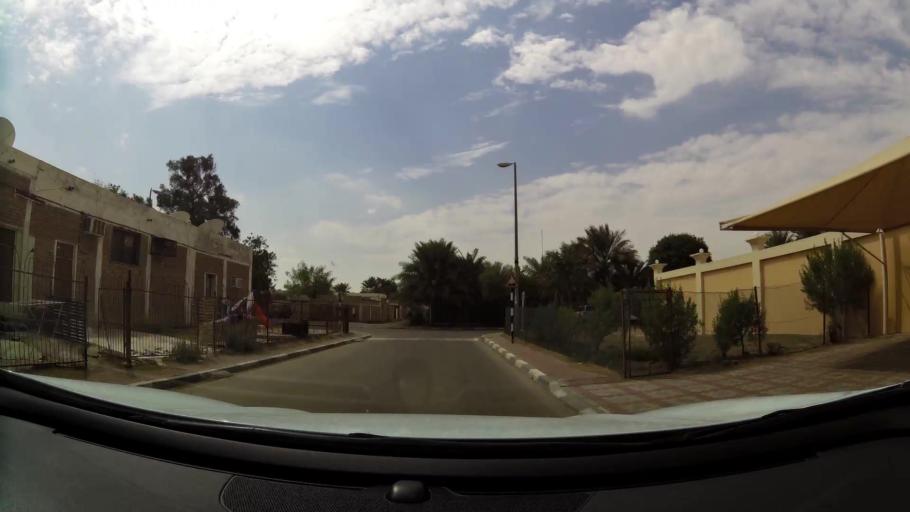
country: AE
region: Abu Dhabi
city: Al Ain
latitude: 24.1982
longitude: 55.7919
